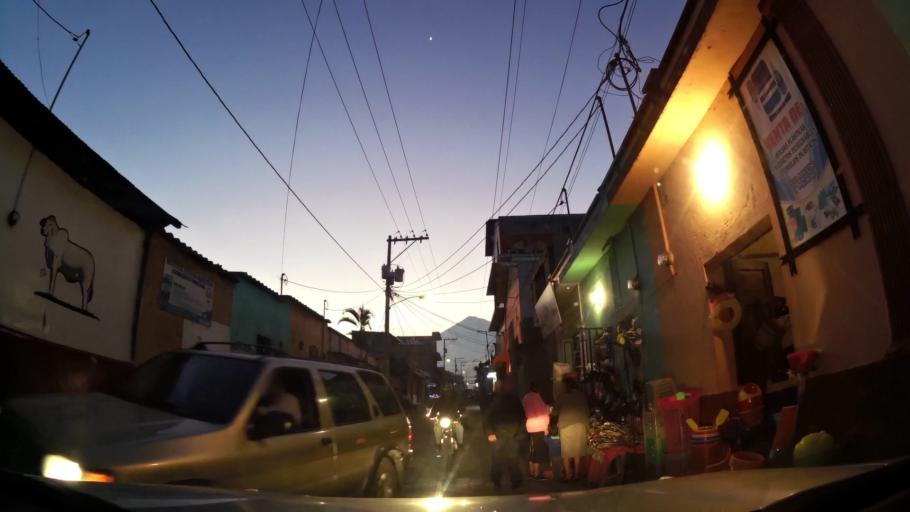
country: GT
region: Sacatepequez
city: Ciudad Vieja
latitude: 14.5236
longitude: -90.7647
